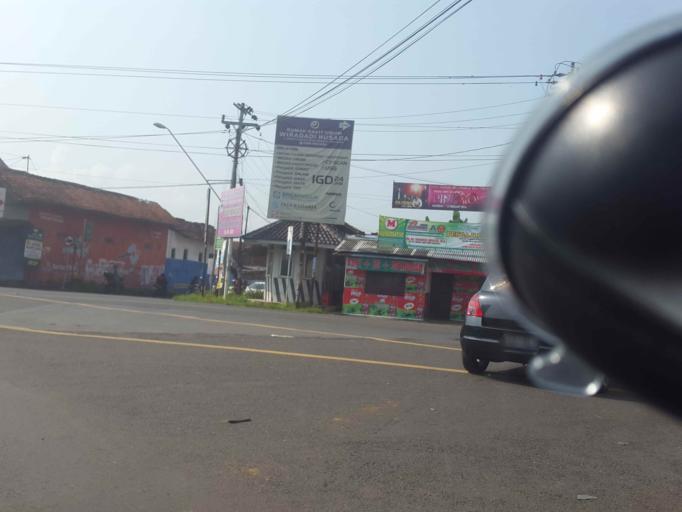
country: ID
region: Central Java
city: Sokaraja
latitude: -7.4573
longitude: 109.2871
